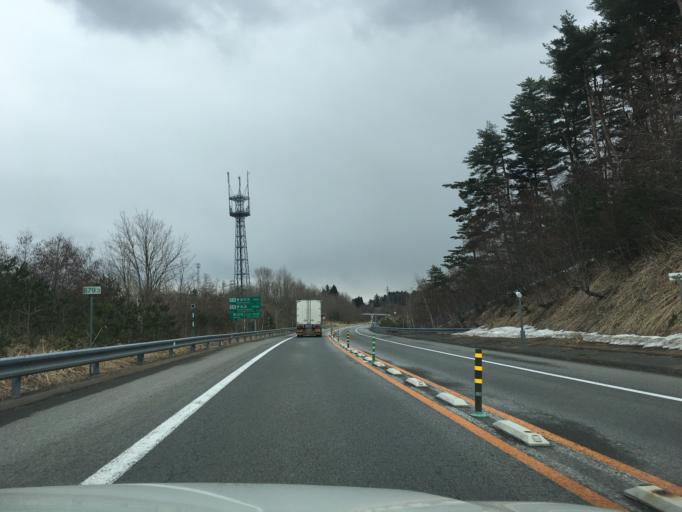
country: JP
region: Aomori
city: Aomori Shi
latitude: 40.8025
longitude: 140.6953
